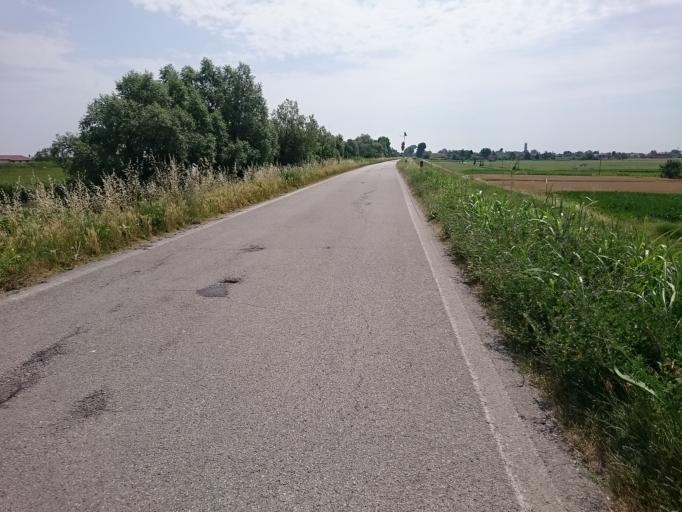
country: IT
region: Veneto
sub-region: Provincia di Padova
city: Correzzola
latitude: 45.2415
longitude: 12.0512
